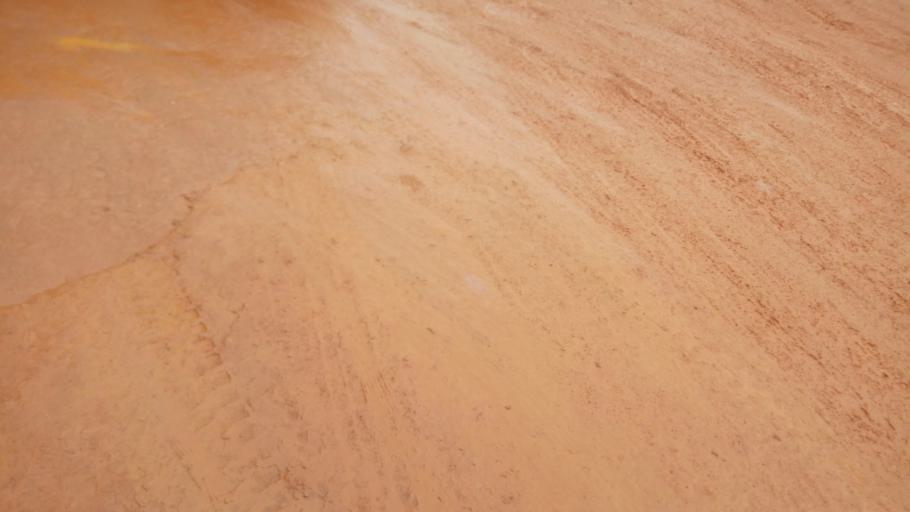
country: GH
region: Ashanti
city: Obuasi
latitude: 6.2125
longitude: -1.6890
